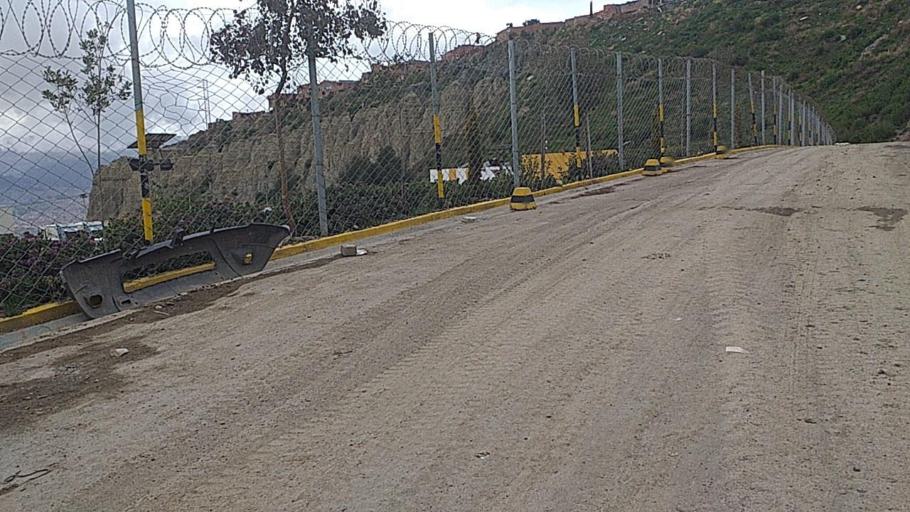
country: BO
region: La Paz
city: La Paz
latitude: -16.5384
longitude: -68.1391
